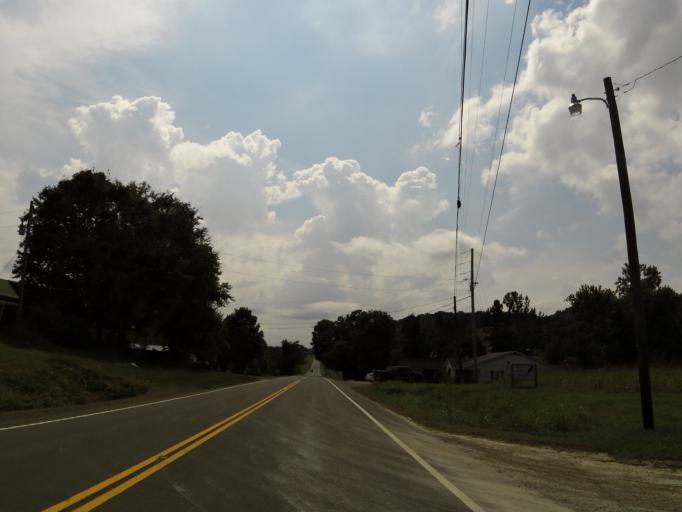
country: US
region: Tennessee
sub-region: Perry County
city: Linden
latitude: 35.7359
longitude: -87.8097
